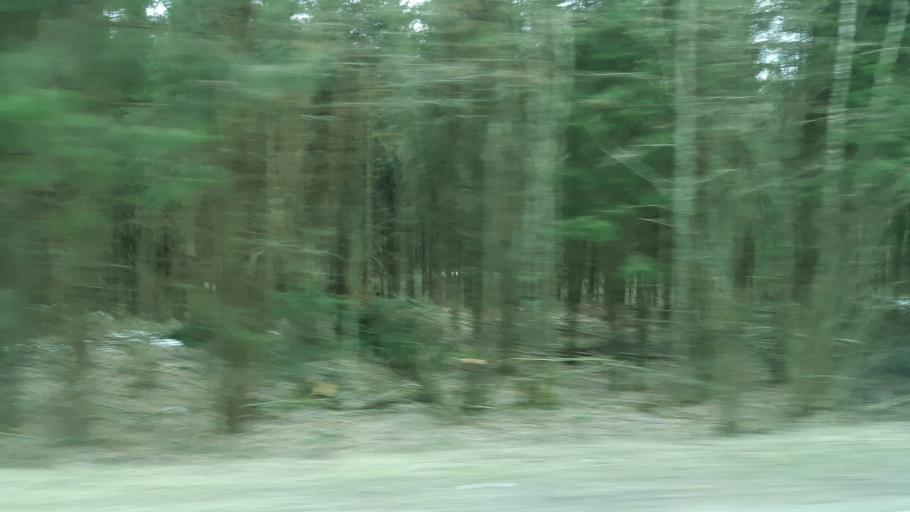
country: PL
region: Podlasie
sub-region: Suwalki
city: Suwalki
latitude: 54.2986
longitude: 22.9573
